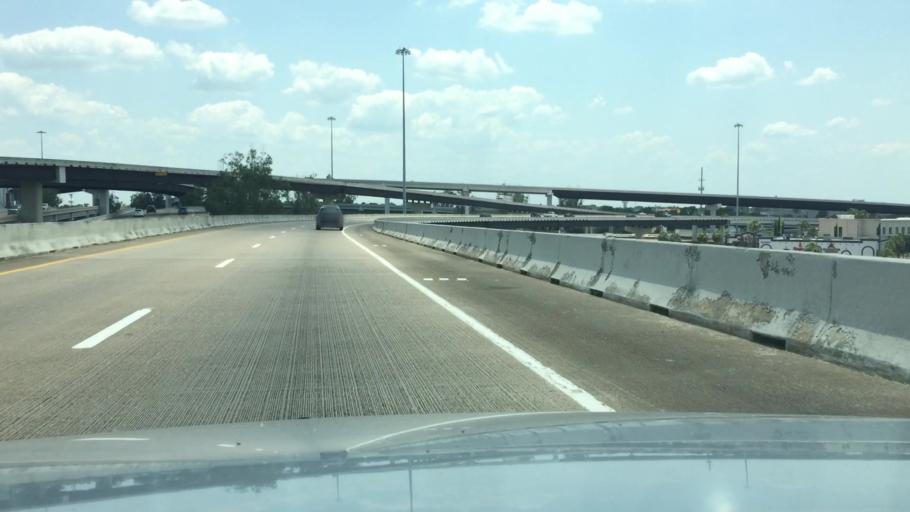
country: US
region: Texas
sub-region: Fort Bend County
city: Meadows Place
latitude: 29.6631
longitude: -95.5594
